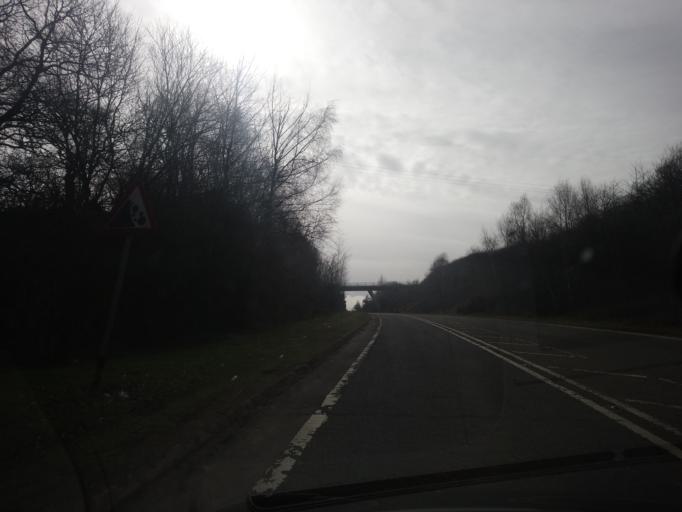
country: GB
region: England
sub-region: Telford and Wrekin
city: Ironbridge
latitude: 52.6497
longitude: -2.5078
